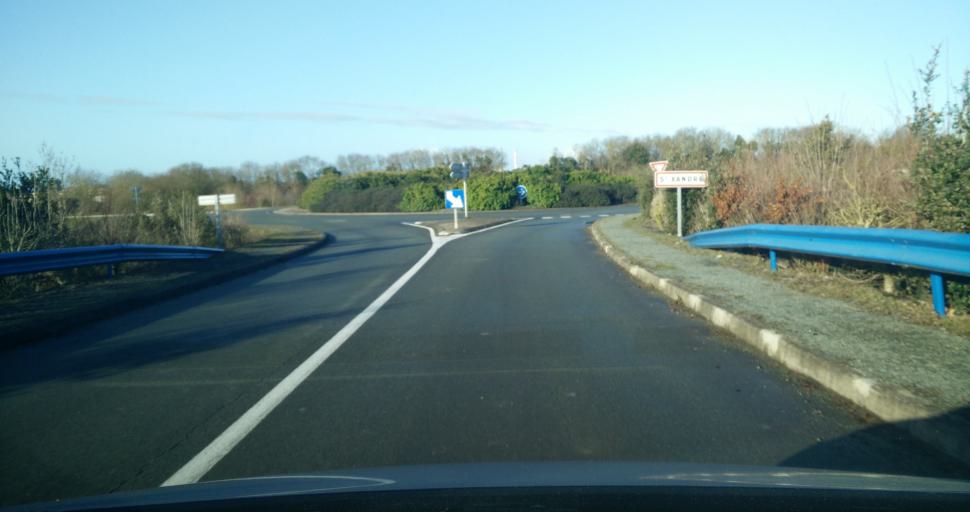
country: FR
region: Poitou-Charentes
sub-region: Departement de la Charente-Maritime
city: Saint-Xandre
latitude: 46.2046
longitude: -1.0904
